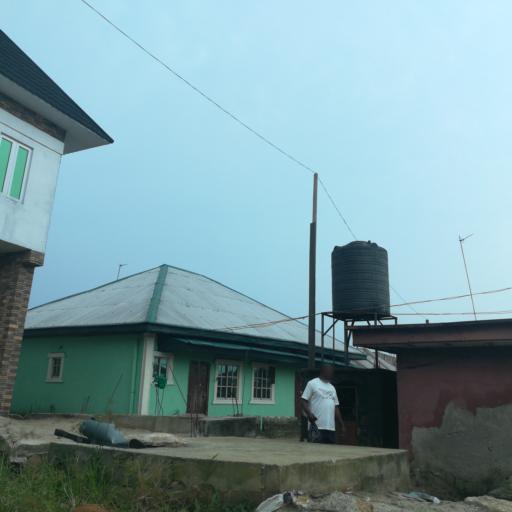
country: NG
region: Rivers
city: Port Harcourt
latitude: 4.7475
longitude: 7.0078
